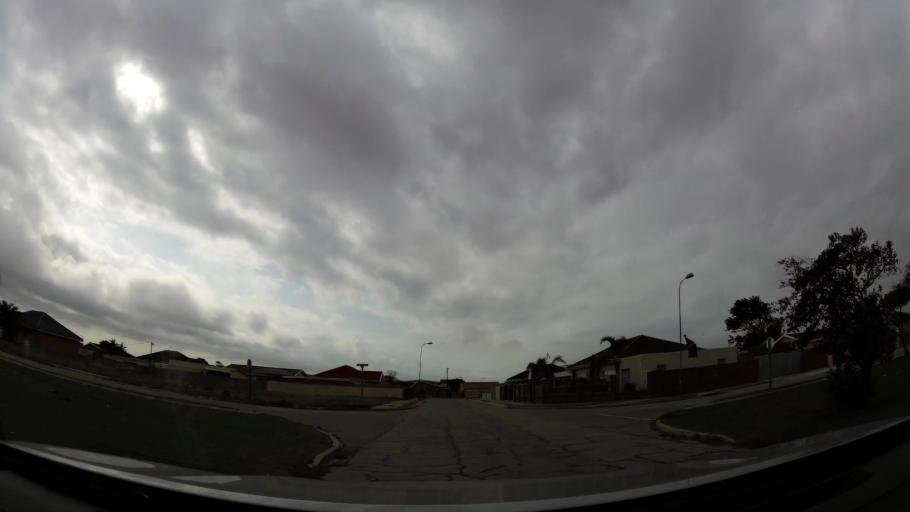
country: ZA
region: Eastern Cape
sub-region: Nelson Mandela Bay Metropolitan Municipality
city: Port Elizabeth
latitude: -33.8990
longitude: 25.5623
